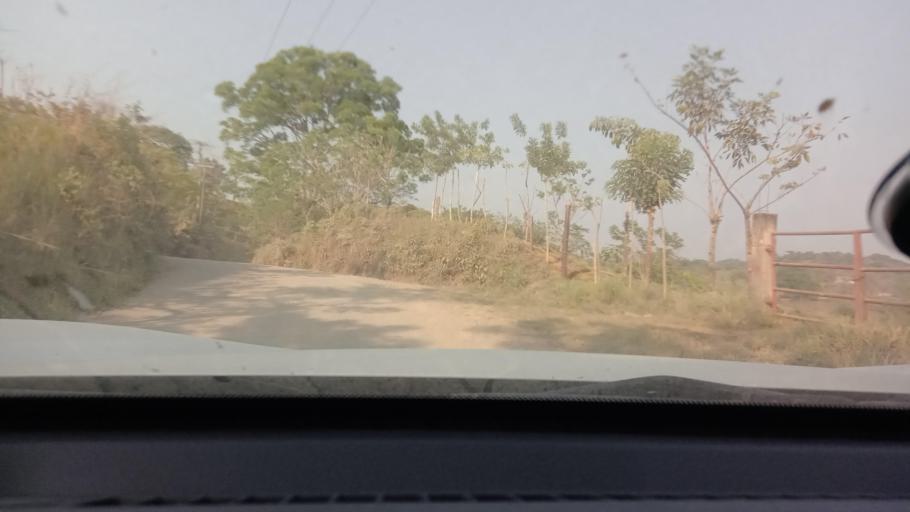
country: MX
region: Tabasco
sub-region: Huimanguillo
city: Francisco Rueda
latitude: 17.6538
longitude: -93.8937
